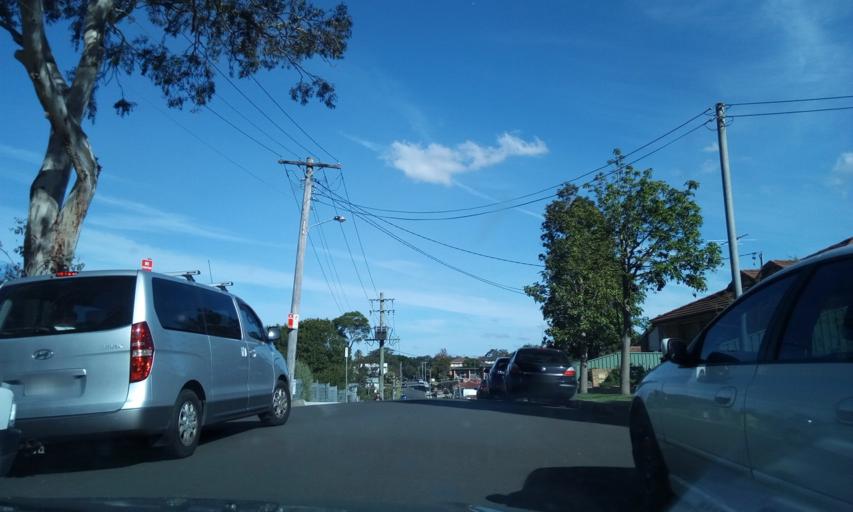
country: AU
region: New South Wales
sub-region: Wollongong
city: Keiraville
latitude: -34.4135
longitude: 150.8725
